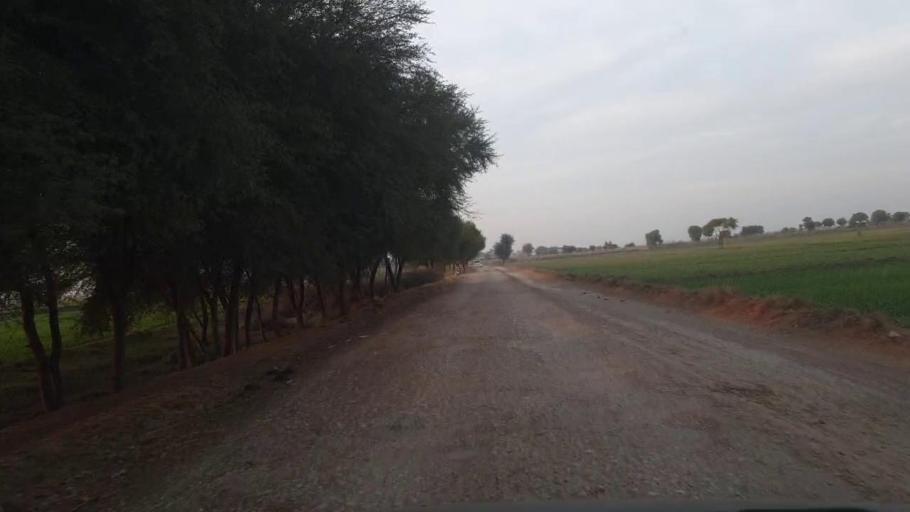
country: PK
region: Sindh
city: Shahpur Chakar
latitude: 26.0688
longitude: 68.5330
